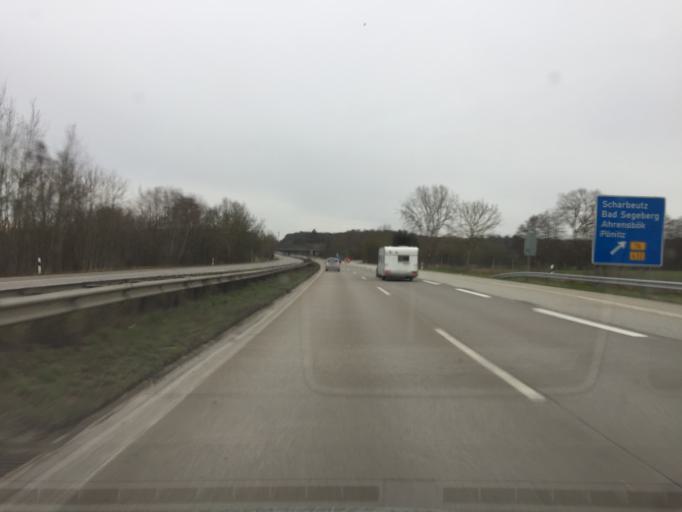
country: DE
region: Schleswig-Holstein
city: Scharbeutz
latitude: 54.0396
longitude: 10.7280
